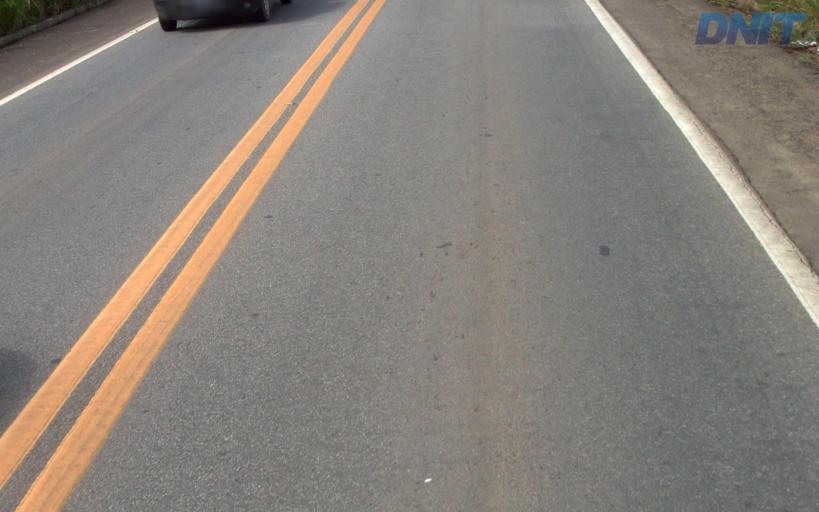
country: BR
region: Minas Gerais
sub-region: Ipaba
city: Ipaba
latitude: -19.3650
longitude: -42.4492
